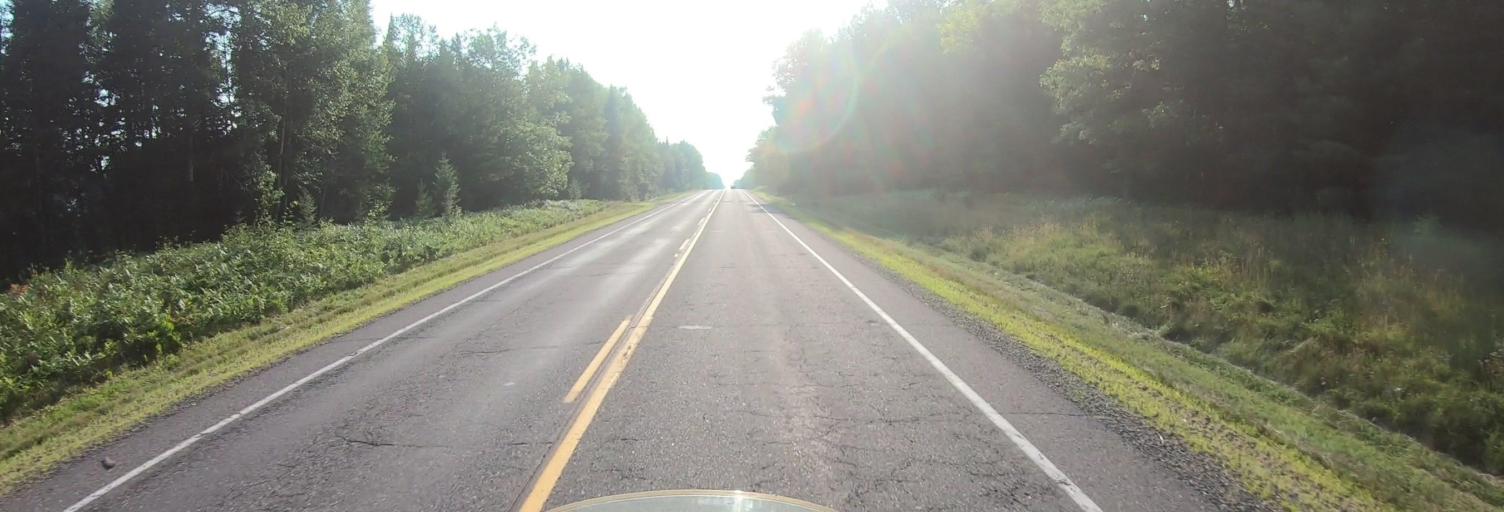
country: US
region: Wisconsin
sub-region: Sawyer County
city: Little Round Lake
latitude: 46.0738
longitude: -91.0646
